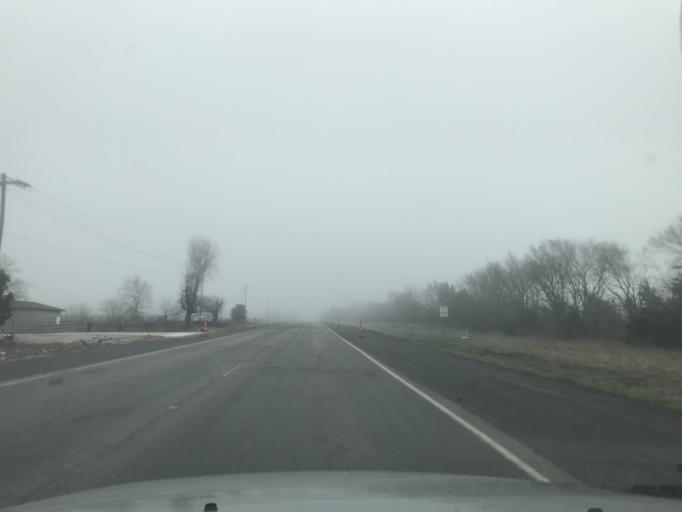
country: US
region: Texas
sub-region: Hunt County
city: Caddo Mills
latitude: 33.0550
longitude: -96.2390
